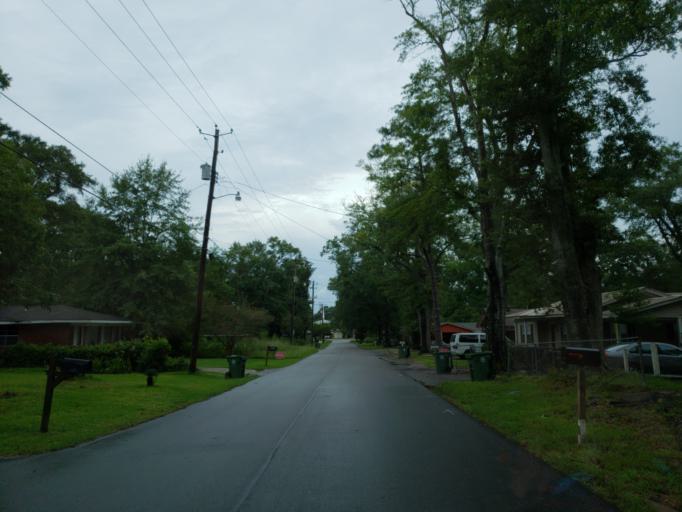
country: US
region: Mississippi
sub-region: Forrest County
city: Hattiesburg
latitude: 31.3082
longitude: -89.2941
